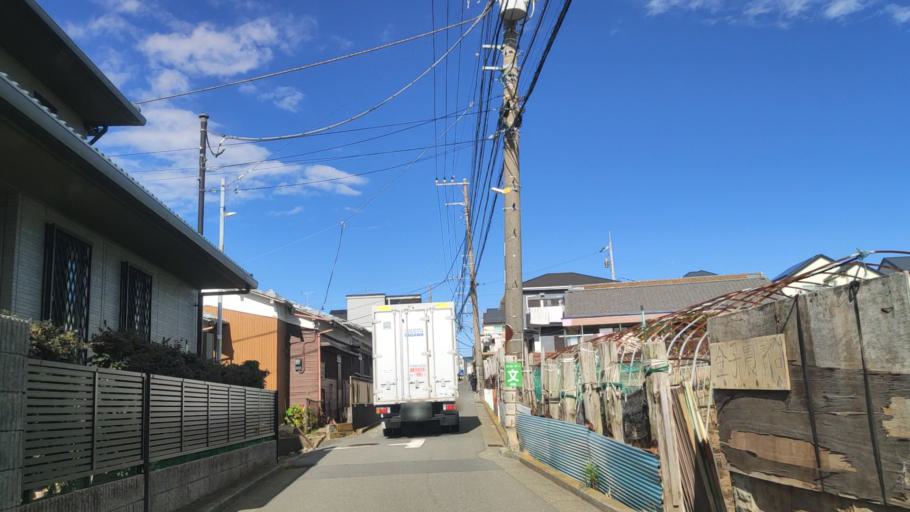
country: JP
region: Kanagawa
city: Yokohama
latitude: 35.4748
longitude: 139.5799
